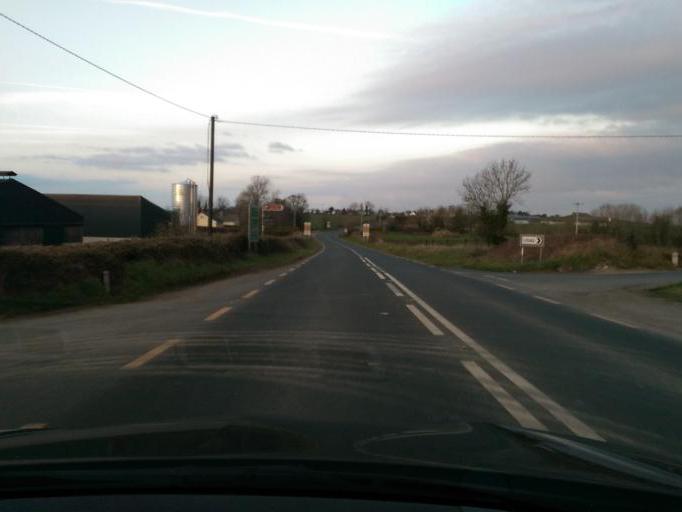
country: IE
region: Munster
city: Nenagh Bridge
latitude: 52.9284
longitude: -8.1661
